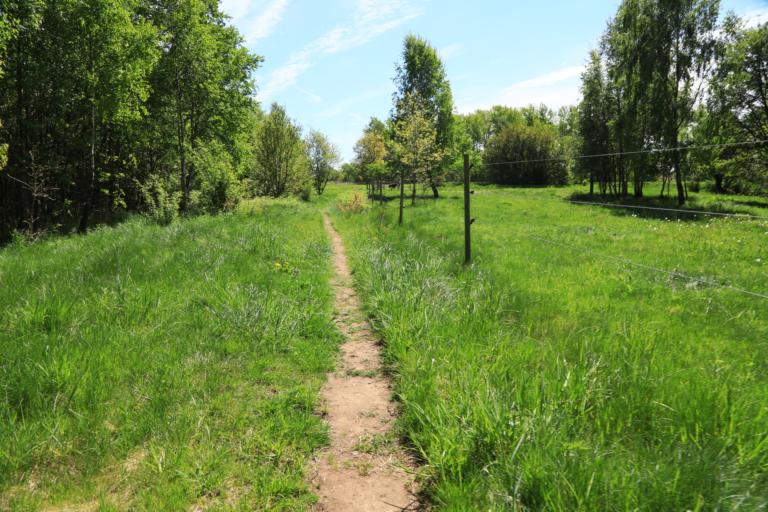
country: SE
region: Halland
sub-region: Varbergs Kommun
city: Varberg
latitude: 57.1156
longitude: 12.3007
